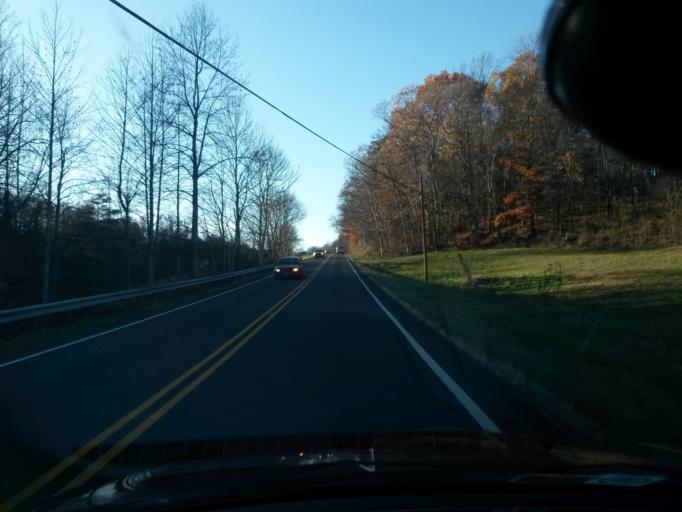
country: US
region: Virginia
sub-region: Amherst County
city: Amherst
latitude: 37.6662
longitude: -79.1659
